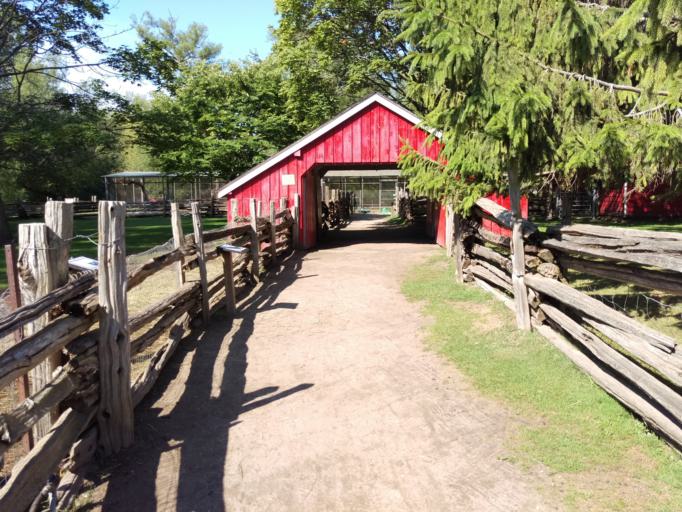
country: CA
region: Ontario
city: Toronto
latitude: 43.6194
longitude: -79.3712
